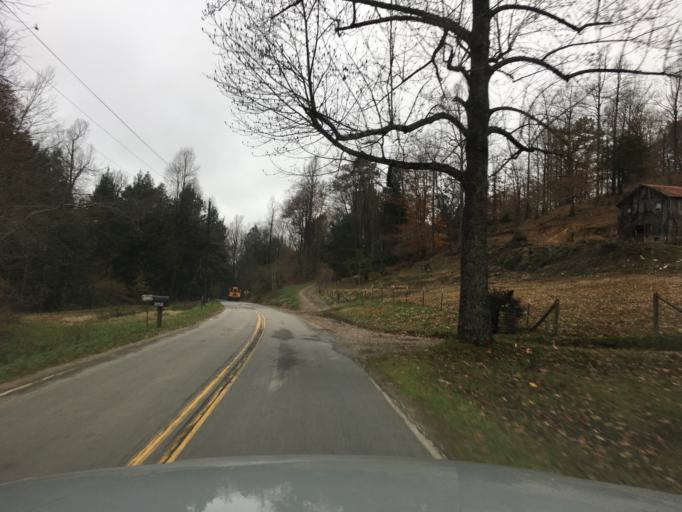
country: US
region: North Carolina
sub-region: Rutherford County
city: Lake Lure
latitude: 35.5256
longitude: -82.2455
